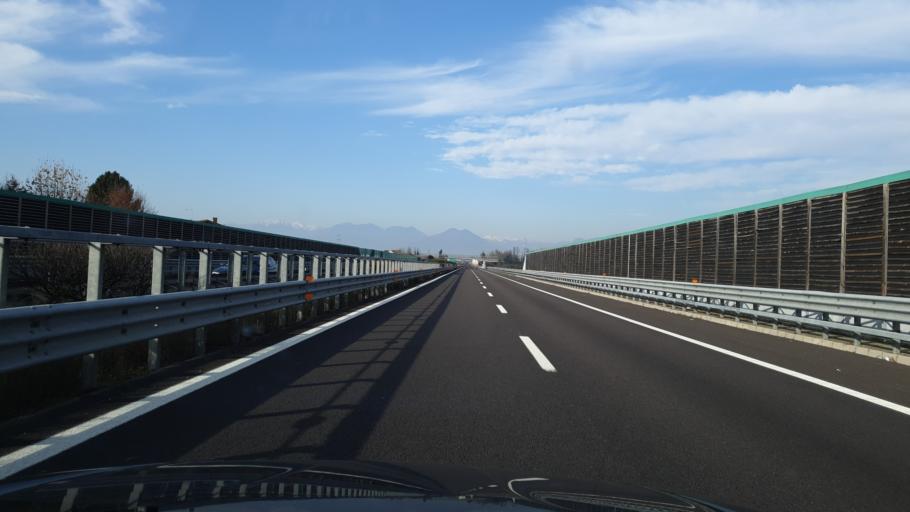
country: IT
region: Veneto
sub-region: Provincia di Vicenza
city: Vigardolo
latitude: 45.6309
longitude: 11.5859
